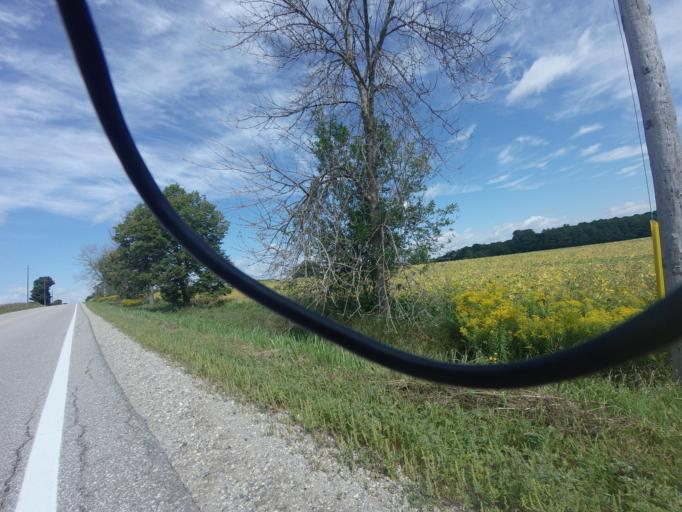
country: CA
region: Ontario
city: Stratford
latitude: 43.4898
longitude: -80.7797
